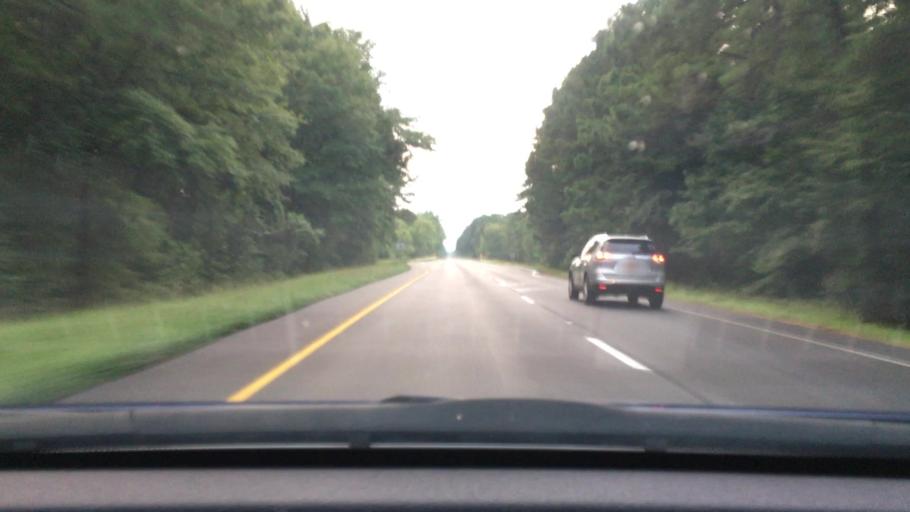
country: US
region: South Carolina
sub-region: Sumter County
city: Stateburg
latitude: 33.9531
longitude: -80.5739
